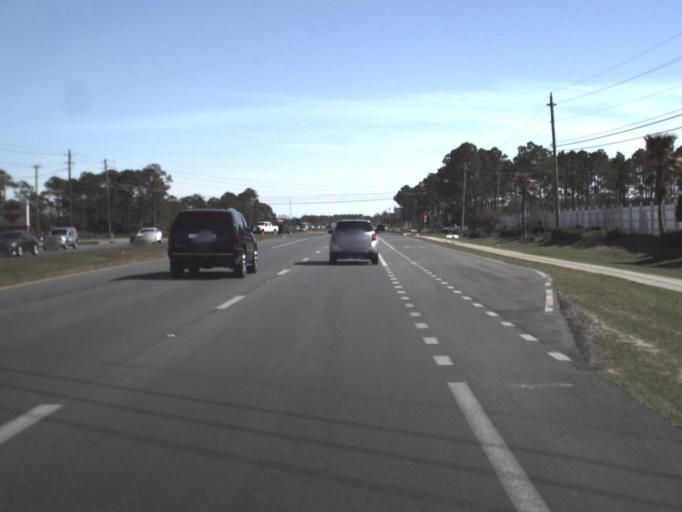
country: US
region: Florida
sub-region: Bay County
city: Panama City Beach
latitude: 30.2141
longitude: -85.8552
